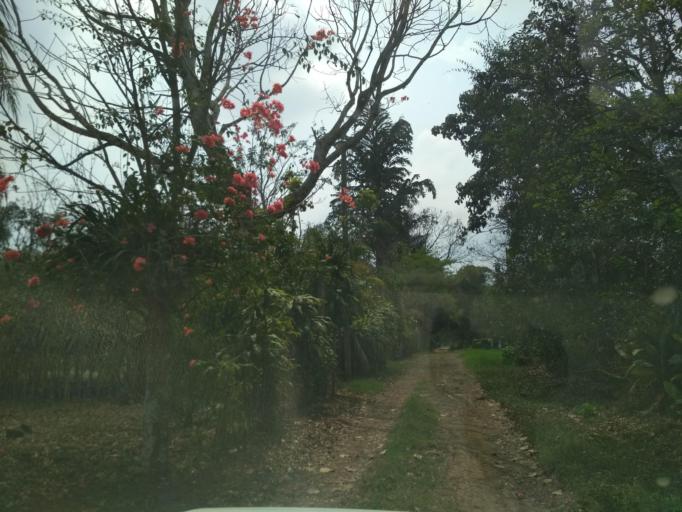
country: MX
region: Veracruz
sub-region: Cordoba
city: San Jose de Tapia
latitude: 18.8545
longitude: -96.9789
